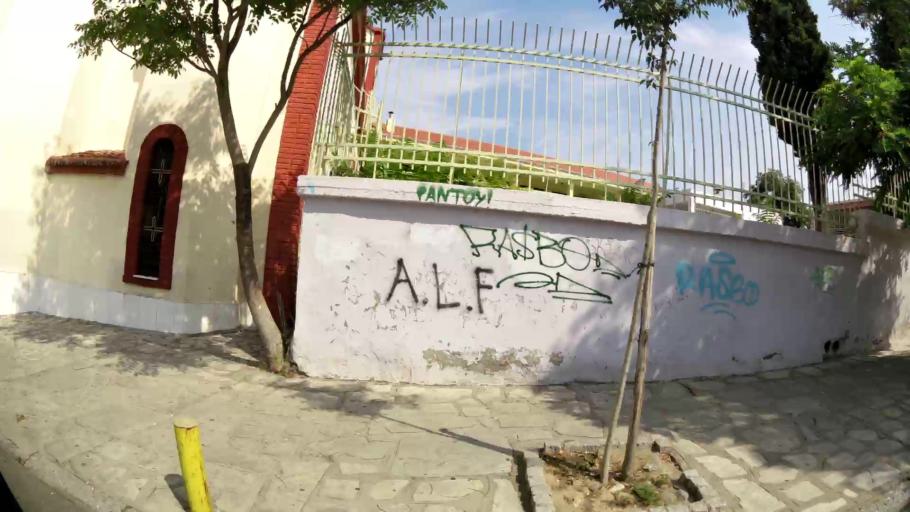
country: GR
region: Central Macedonia
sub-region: Nomos Thessalonikis
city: Agios Pavlos
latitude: 40.6416
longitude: 22.9596
